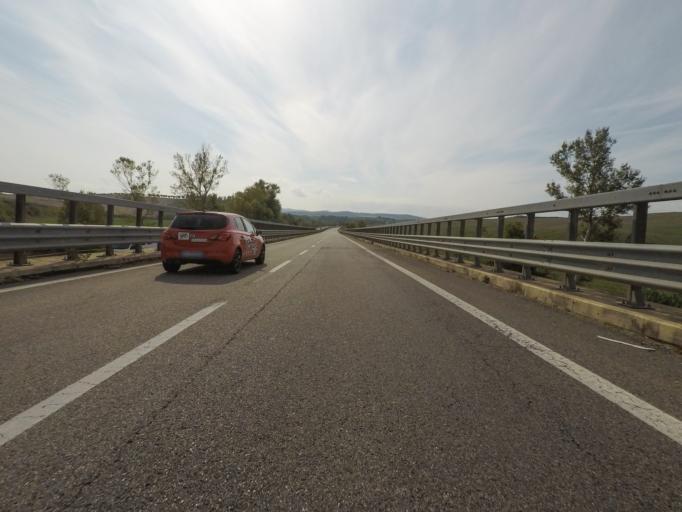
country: IT
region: Tuscany
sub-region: Provincia di Siena
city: Isola D'Arbia
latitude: 43.2653
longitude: 11.3290
